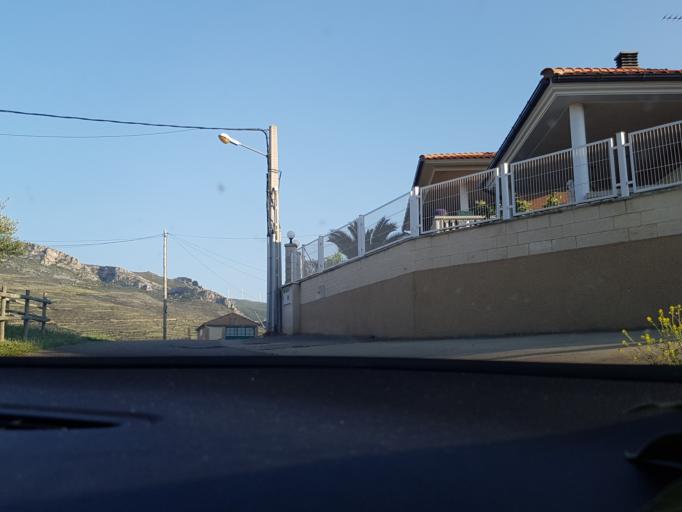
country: ES
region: La Rioja
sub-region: Provincia de La Rioja
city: Prejano
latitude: 42.1874
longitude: -2.1817
